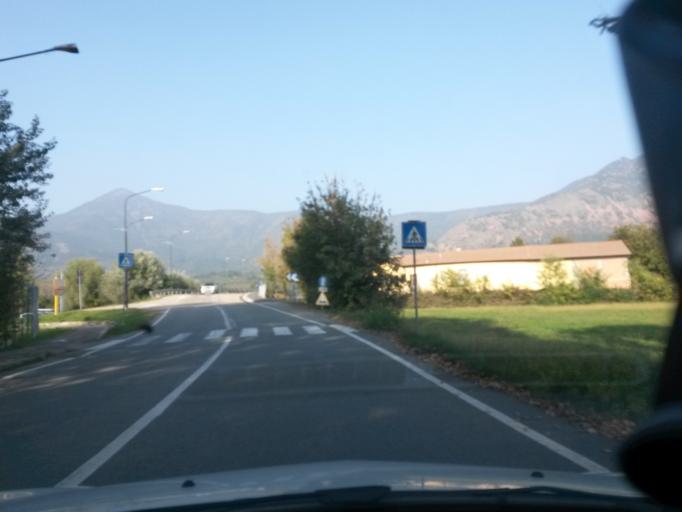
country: IT
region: Piedmont
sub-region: Provincia di Torino
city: Drubiaglio-Grangia
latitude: 45.0956
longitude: 7.4159
